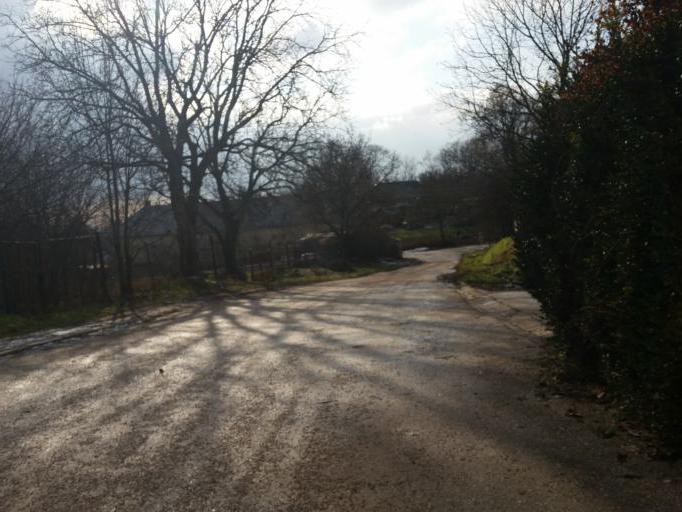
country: SK
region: Trnavsky
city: Vrbove
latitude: 48.6586
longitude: 17.7168
